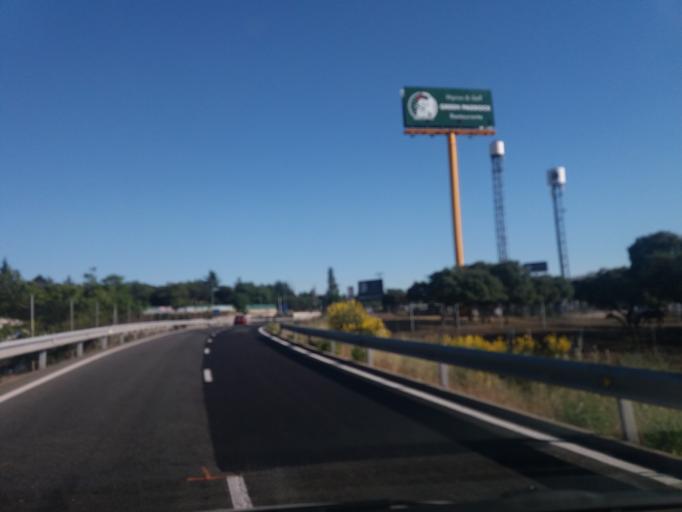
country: ES
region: Madrid
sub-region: Provincia de Madrid
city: Torrelodones
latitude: 40.5944
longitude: -3.9531
